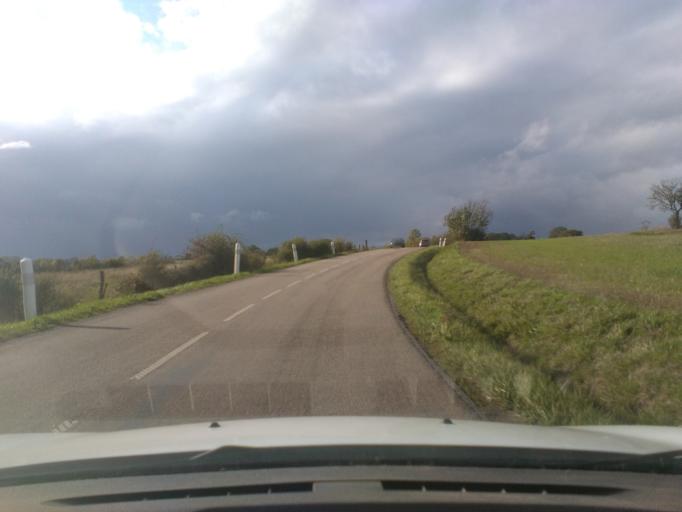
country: FR
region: Lorraine
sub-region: Departement des Vosges
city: Aydoilles
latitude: 48.2525
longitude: 6.5850
